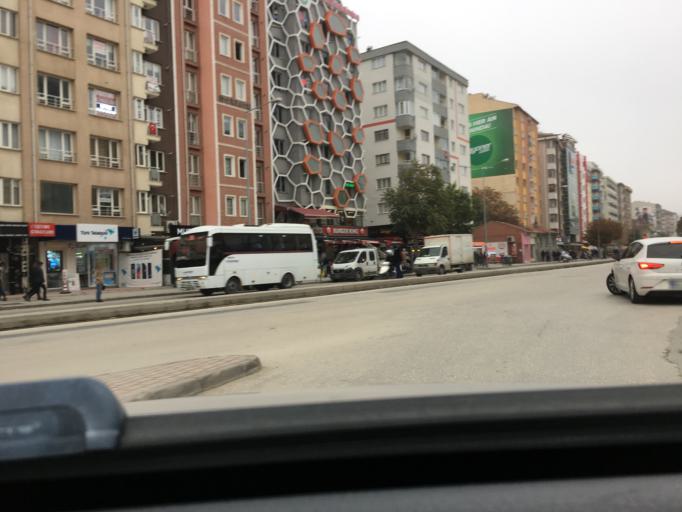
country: TR
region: Eskisehir
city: Eskisehir
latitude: 39.7838
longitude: 30.5107
